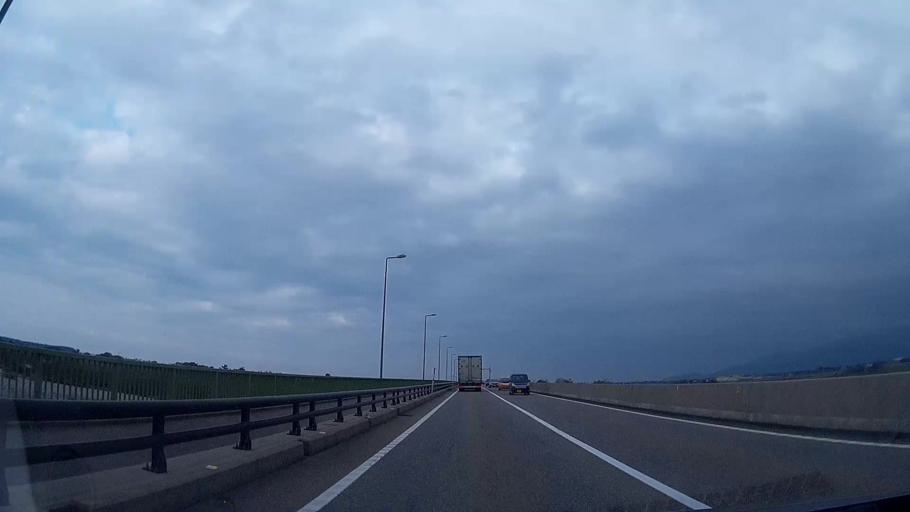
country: JP
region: Toyama
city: Nyuzen
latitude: 36.9031
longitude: 137.4491
